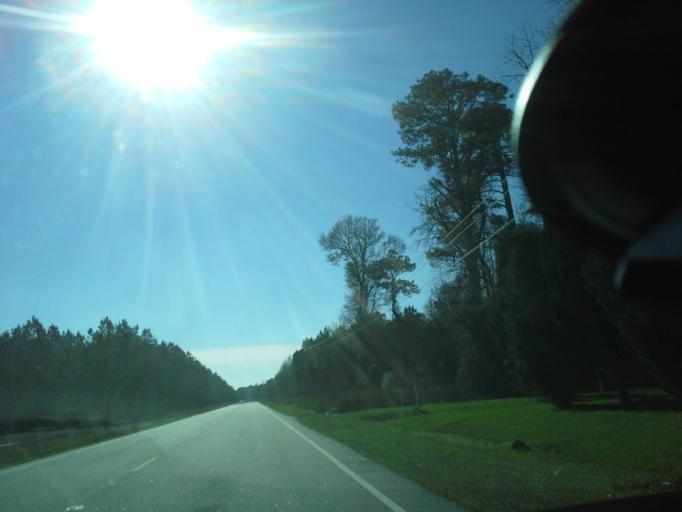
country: US
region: North Carolina
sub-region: Beaufort County
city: Belhaven
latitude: 35.5589
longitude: -76.7002
